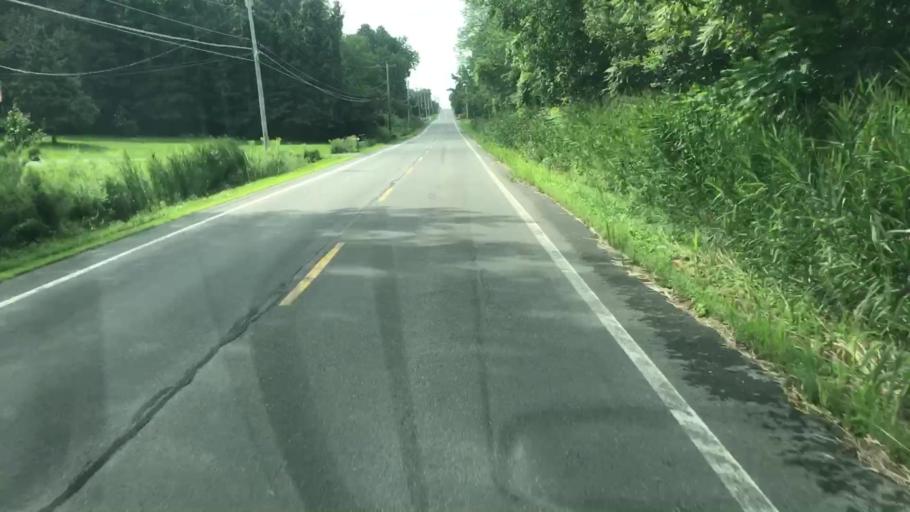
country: US
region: New York
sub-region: Onondaga County
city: Peru
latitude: 43.0498
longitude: -76.3662
